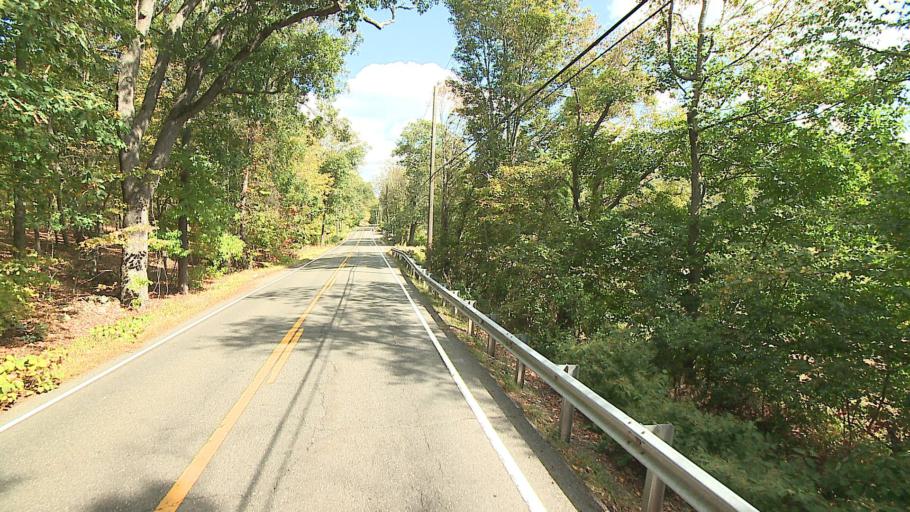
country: US
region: Connecticut
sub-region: New Haven County
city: Naugatuck
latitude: 41.4517
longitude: -73.0140
